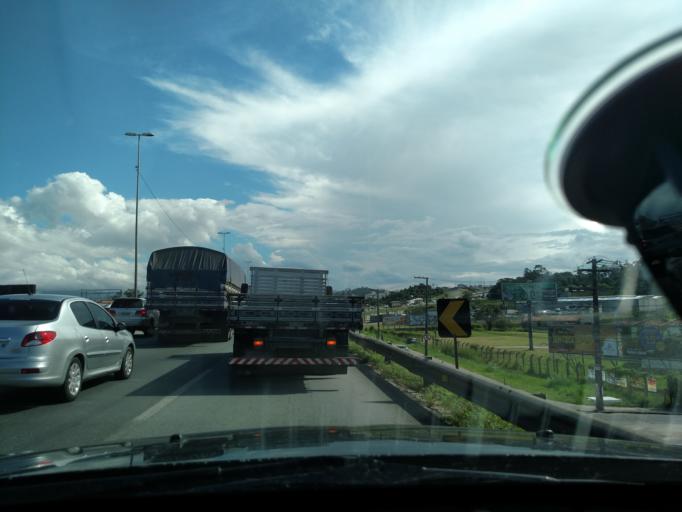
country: BR
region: Santa Catarina
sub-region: Sao Jose
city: Campinas
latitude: -27.5990
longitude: -48.6217
